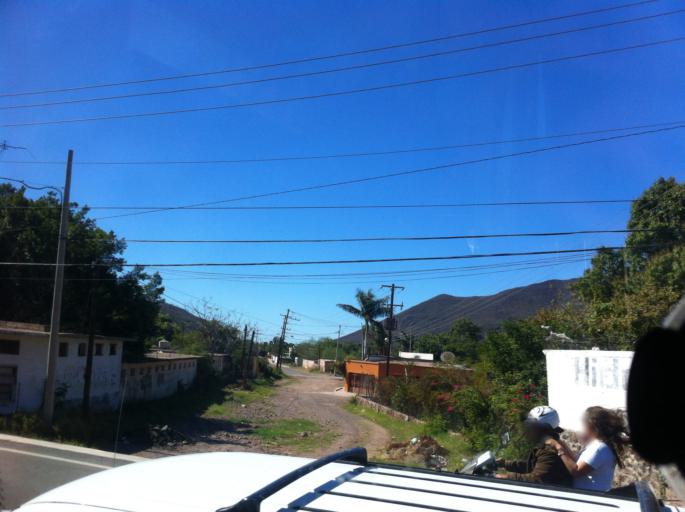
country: MX
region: Sonora
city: Heroica Guaymas
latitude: 27.9420
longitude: -110.9327
